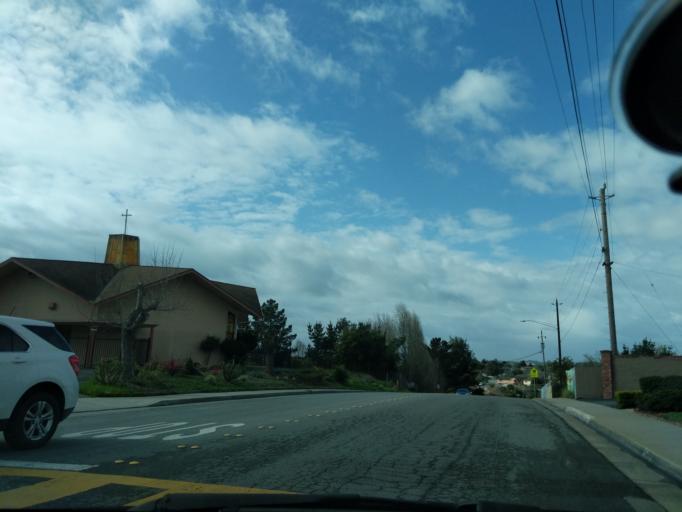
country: US
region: California
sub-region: Santa Cruz County
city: Freedom
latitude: 36.9224
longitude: -121.7702
